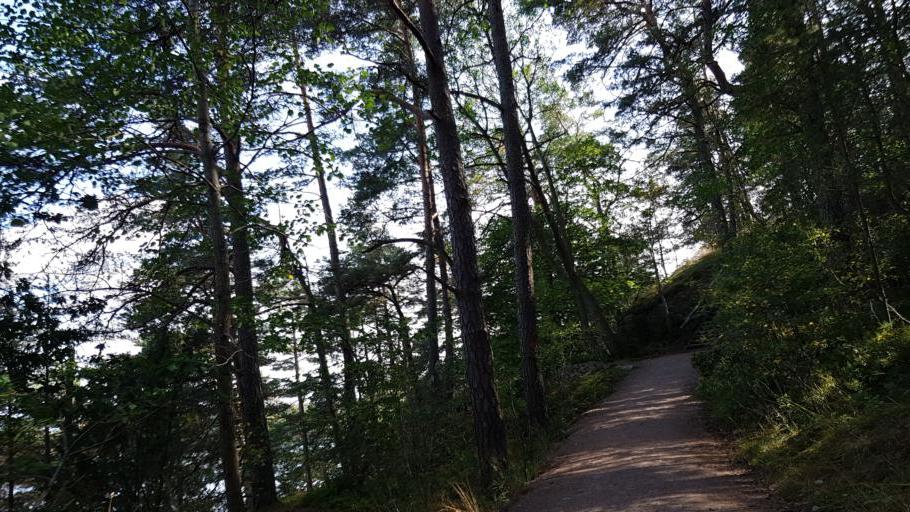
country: SE
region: Vaestra Goetaland
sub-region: Molndal
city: Moelndal
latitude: 57.6869
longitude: 12.0344
